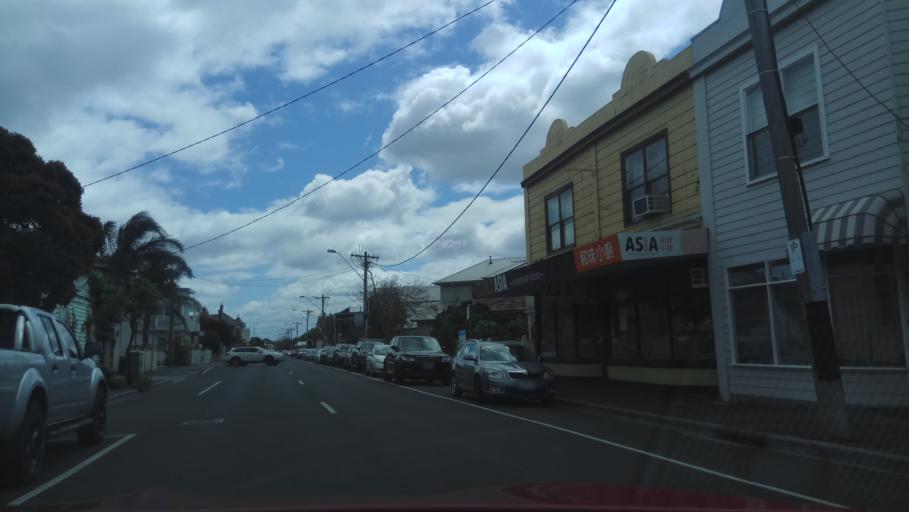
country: AU
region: Victoria
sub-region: Hobsons Bay
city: Williamstown
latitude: -37.8549
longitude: 144.8973
